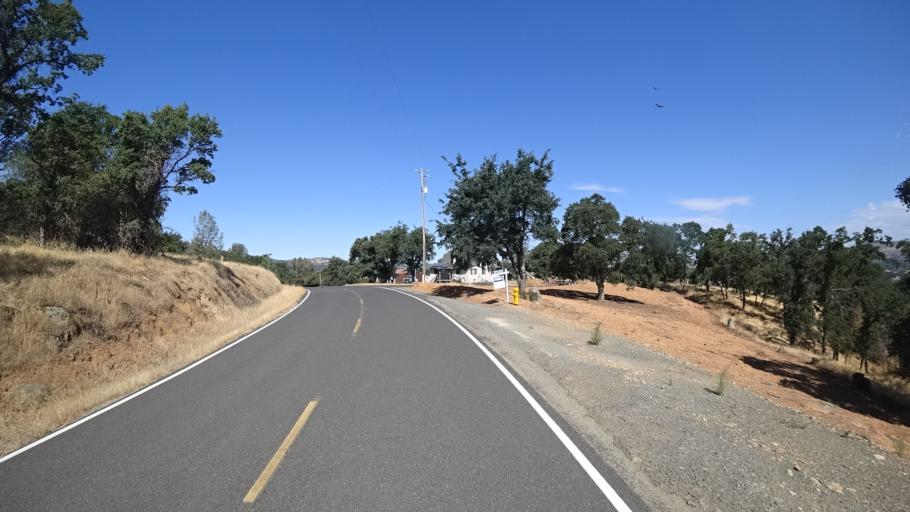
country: US
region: California
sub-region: Calaveras County
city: Copperopolis
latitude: 37.9333
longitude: -120.6331
